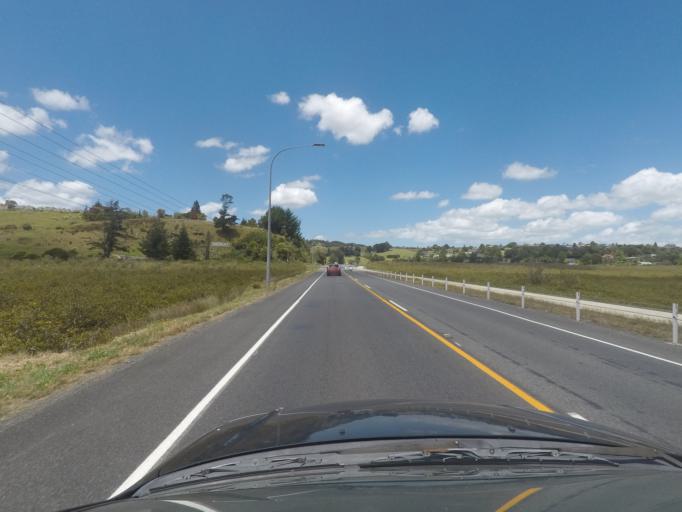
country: NZ
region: Northland
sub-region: Whangarei
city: Whangarei
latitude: -35.7380
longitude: 174.3572
